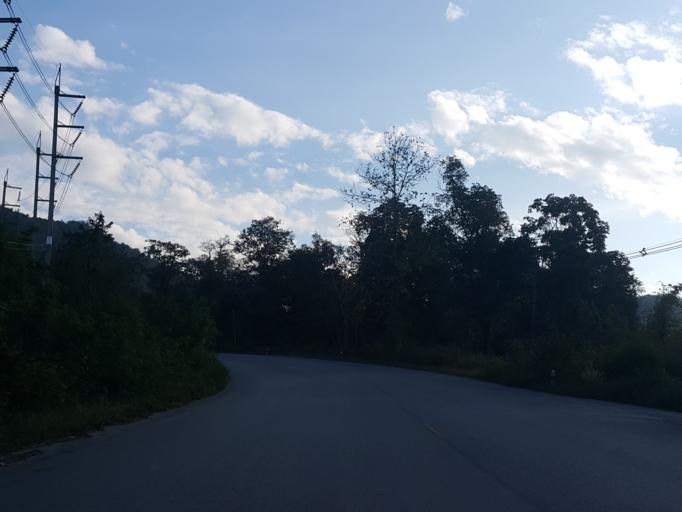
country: TH
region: Lampang
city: Chae Hom
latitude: 18.5164
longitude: 99.5551
